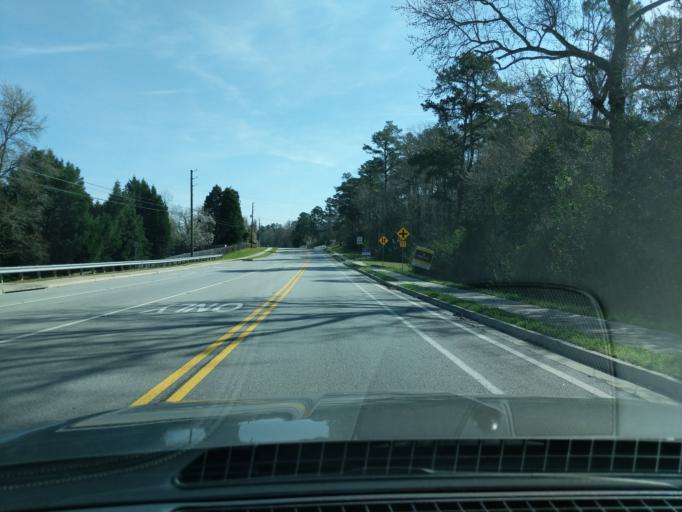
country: US
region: Georgia
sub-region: Columbia County
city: Evans
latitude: 33.5299
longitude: -82.1510
